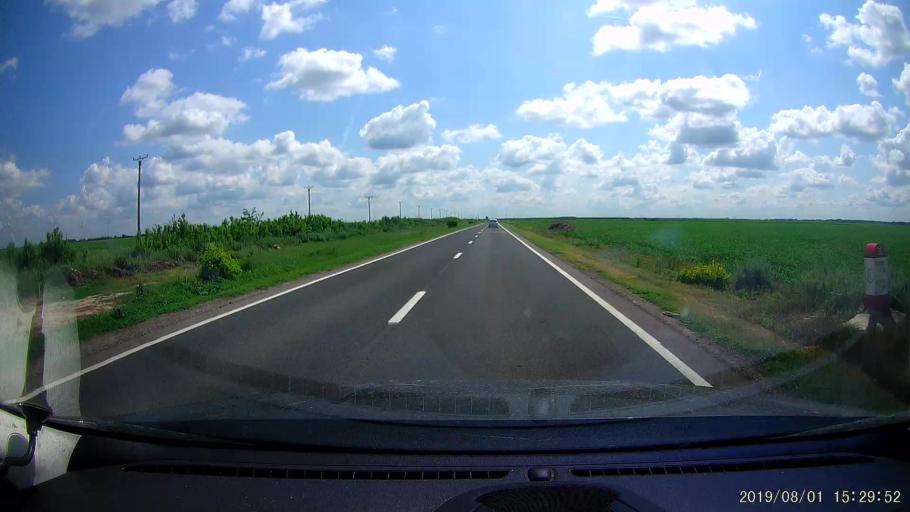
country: RO
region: Braila
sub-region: Comuna Viziru
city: Viziru
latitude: 44.9742
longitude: 27.6887
